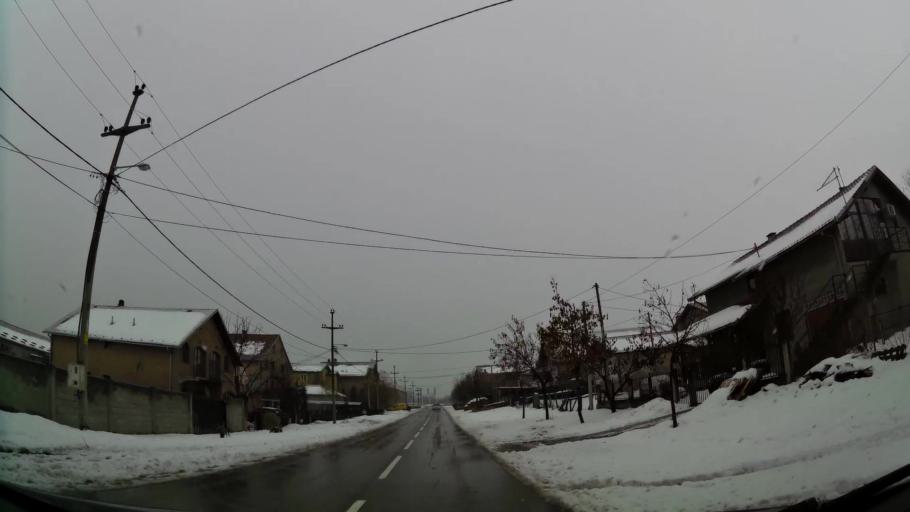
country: RS
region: Central Serbia
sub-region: Belgrade
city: Zemun
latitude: 44.8464
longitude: 20.3461
